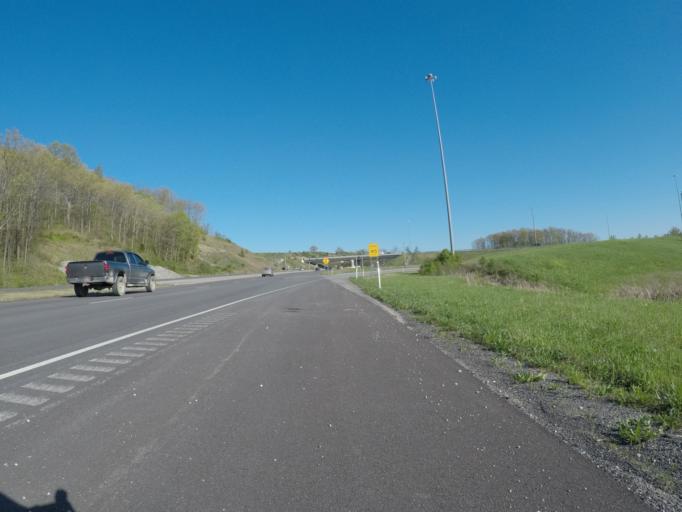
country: US
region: Kentucky
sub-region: Boyd County
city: Meads
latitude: 38.3711
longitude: -82.7013
